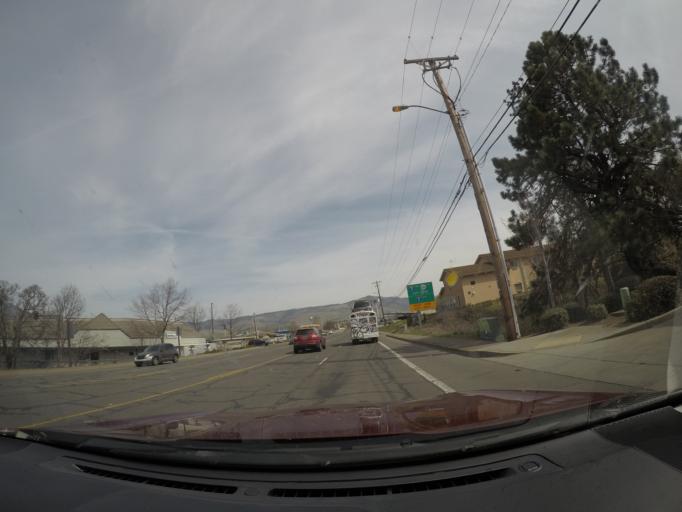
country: US
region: Oregon
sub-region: Jackson County
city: Ashland
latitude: 42.1853
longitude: -122.6701
